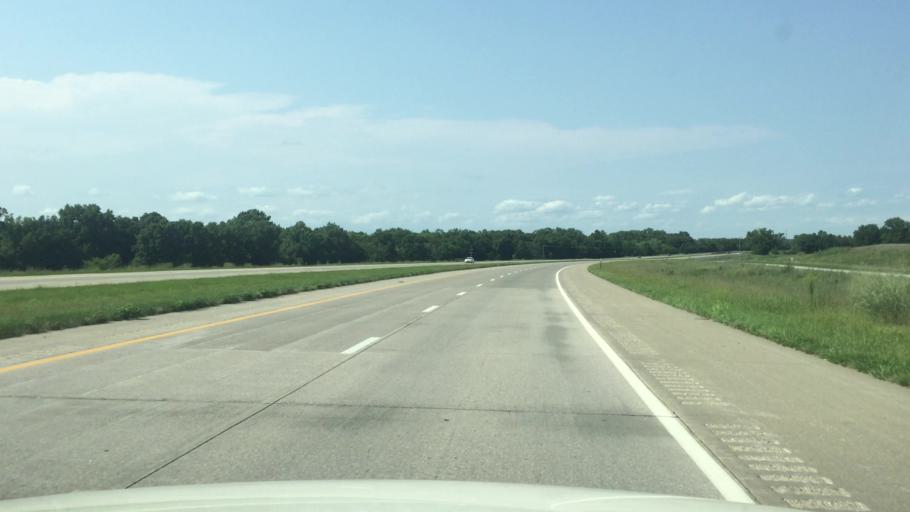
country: US
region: Kansas
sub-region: Linn County
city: La Cygne
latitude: 38.2921
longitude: -94.6761
